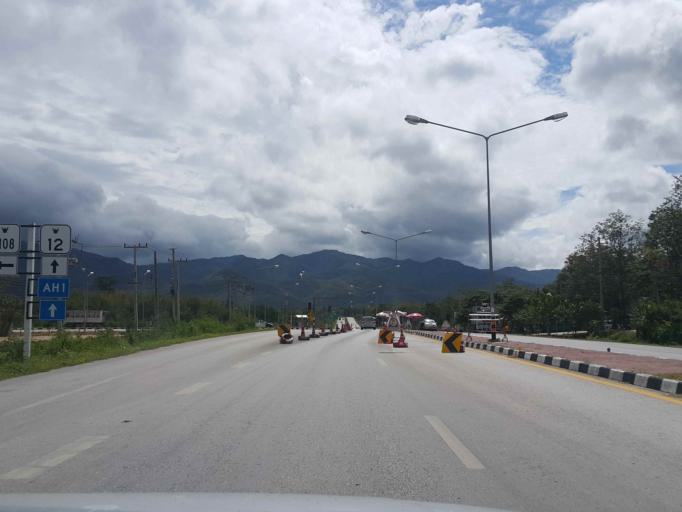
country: TH
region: Tak
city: Tak
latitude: 16.8039
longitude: 99.0441
